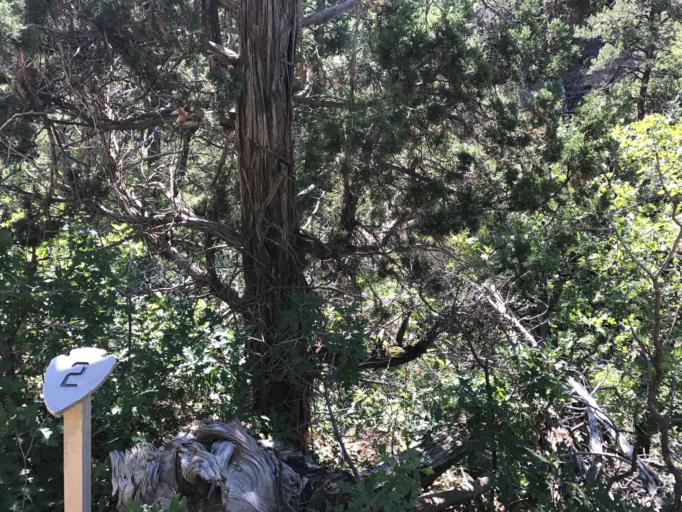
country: US
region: Colorado
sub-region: Montezuma County
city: Cortez
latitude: 37.1829
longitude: -108.4878
